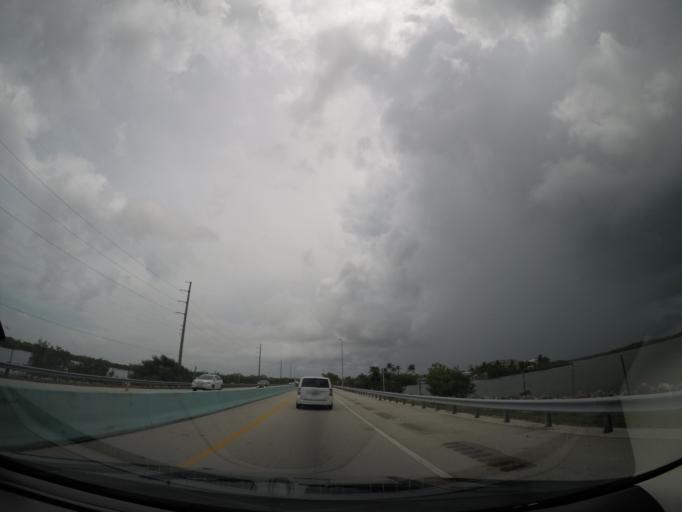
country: US
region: Florida
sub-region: Monroe County
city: North Key Largo
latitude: 25.2304
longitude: -80.4322
